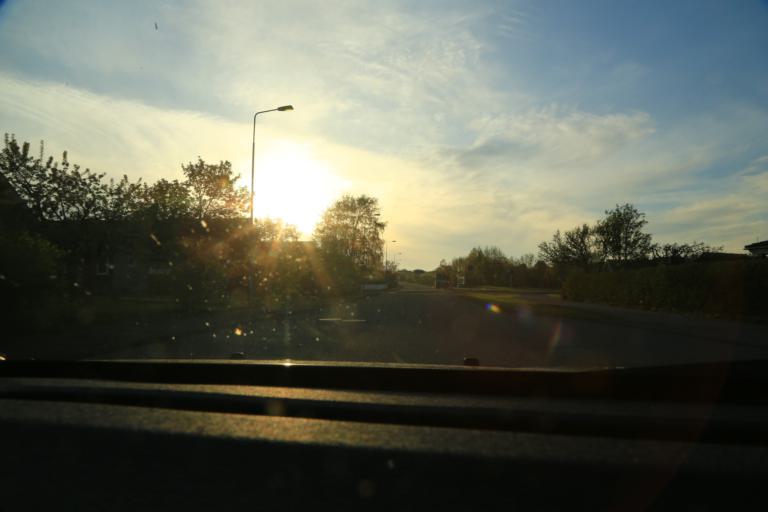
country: SE
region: Halland
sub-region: Varbergs Kommun
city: Traslovslage
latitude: 57.0506
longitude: 12.2881
